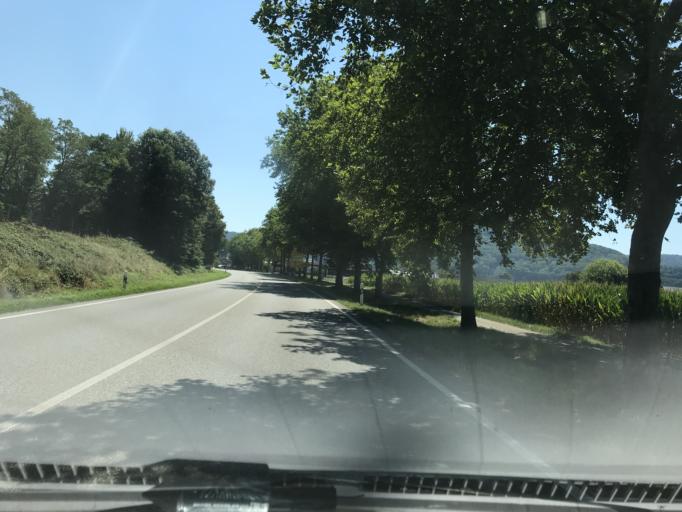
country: CH
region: Aargau
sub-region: Bezirk Rheinfelden
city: Mumpf
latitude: 47.5567
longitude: 7.9279
